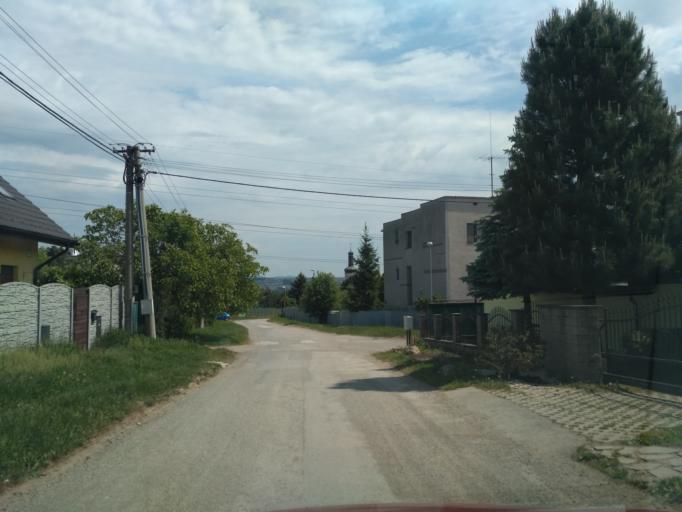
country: SK
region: Kosicky
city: Kosice
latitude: 48.7276
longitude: 21.2294
